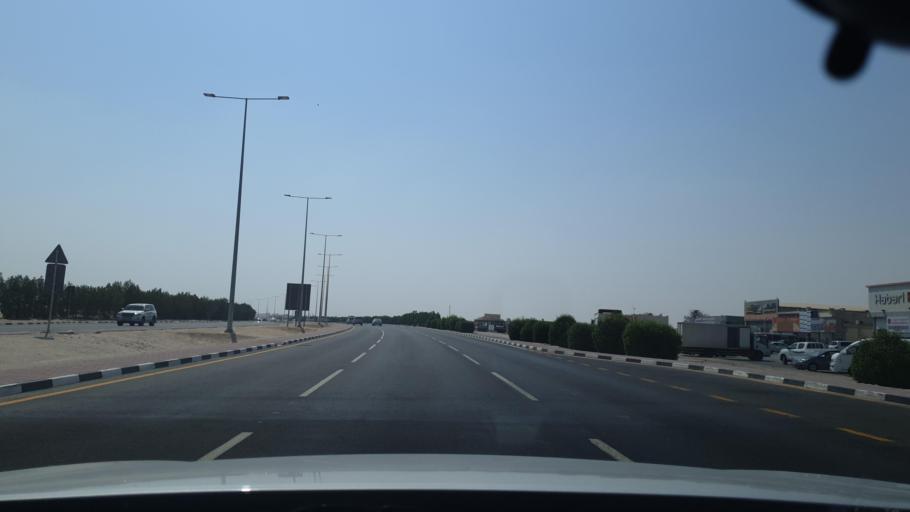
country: QA
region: Al Khawr
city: Al Khawr
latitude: 25.7121
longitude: 51.5068
